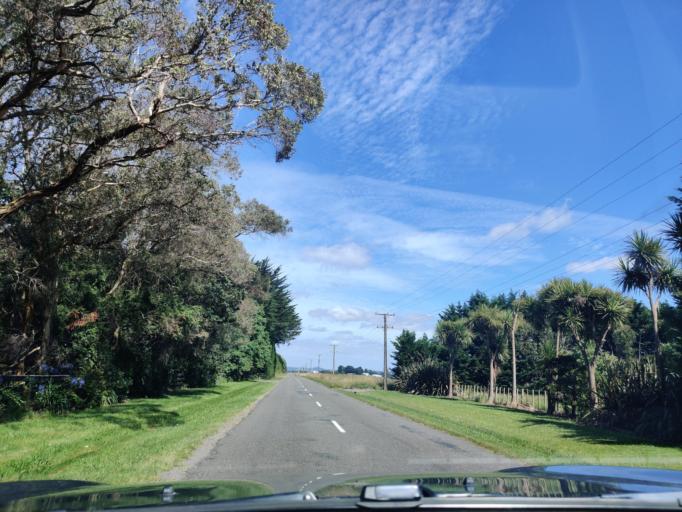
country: NZ
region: Manawatu-Wanganui
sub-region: Rangitikei District
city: Bulls
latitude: -40.1873
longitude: 175.4530
